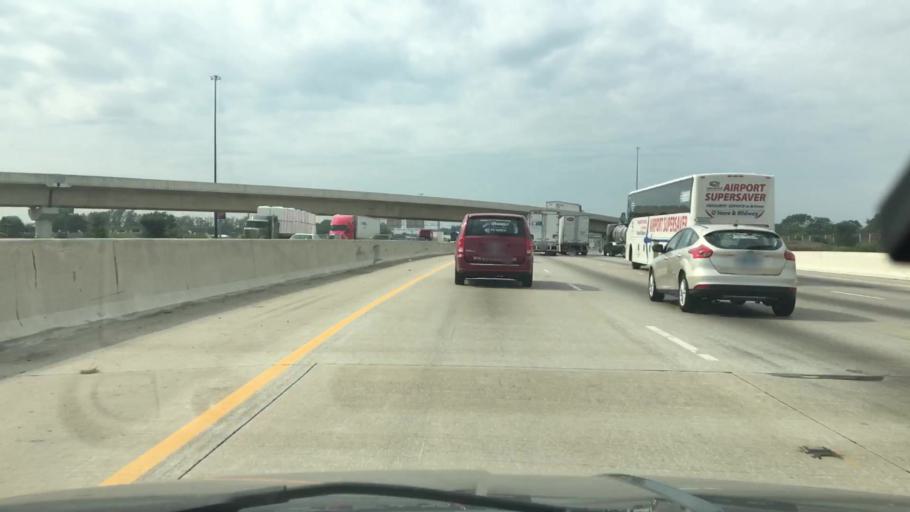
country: US
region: Indiana
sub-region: Lake County
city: Highland
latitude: 41.5701
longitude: -87.4321
